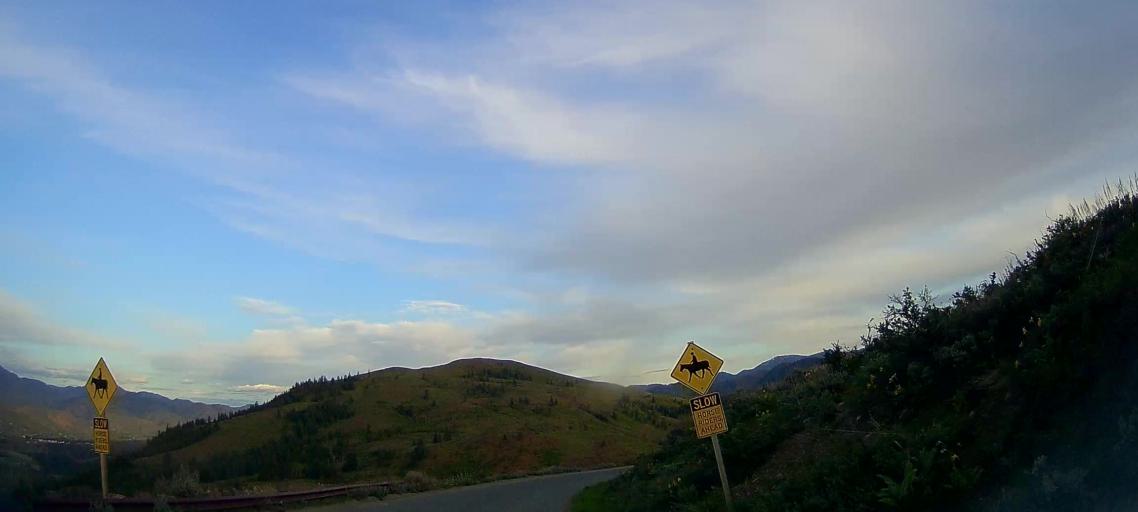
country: US
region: Washington
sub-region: Chelan County
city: Granite Falls
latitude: 48.4758
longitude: -120.2532
